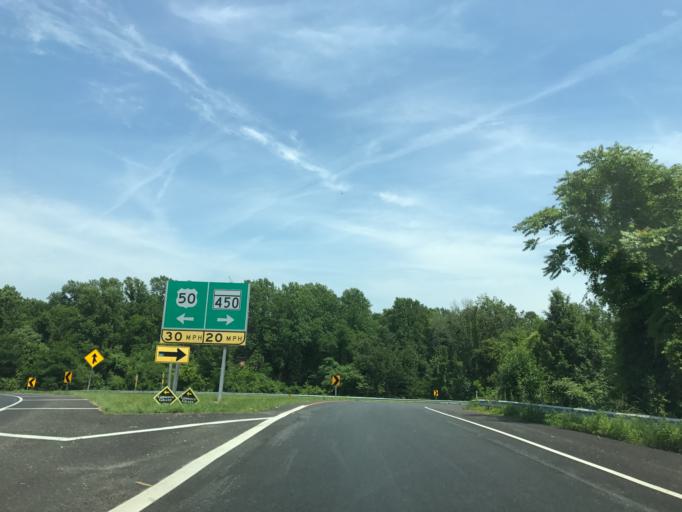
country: US
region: Maryland
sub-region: Anne Arundel County
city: Arnold
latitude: 39.0142
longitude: -76.4901
